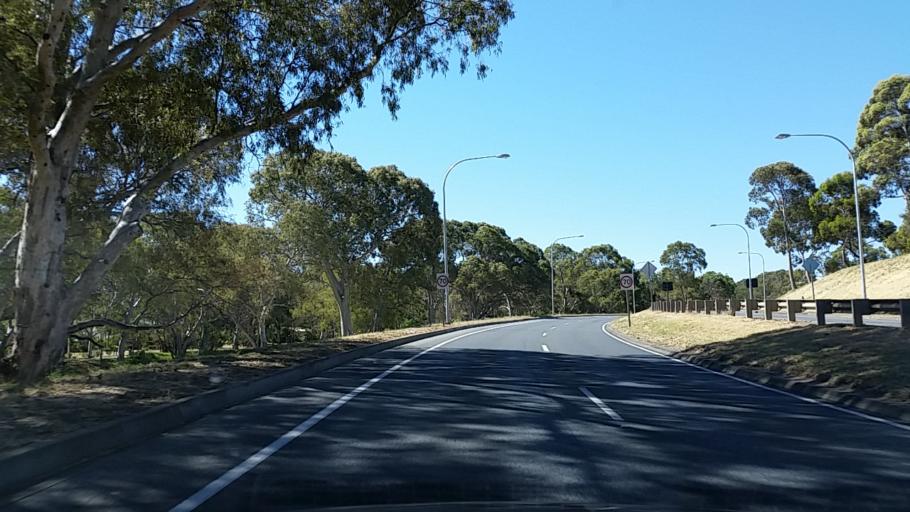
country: AU
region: South Australia
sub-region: Tea Tree Gully
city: Hope Valley
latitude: -34.8155
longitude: 138.6939
